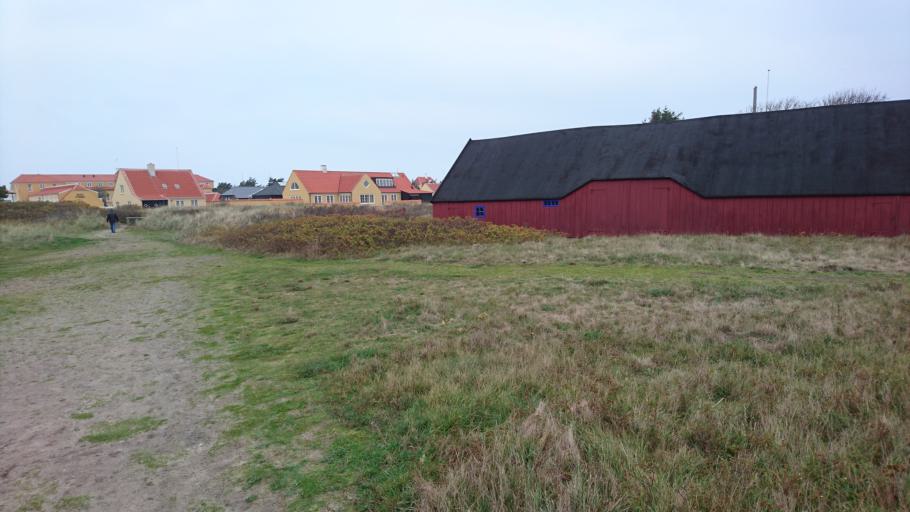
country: DK
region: North Denmark
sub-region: Frederikshavn Kommune
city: Skagen
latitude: 57.7258
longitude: 10.5218
